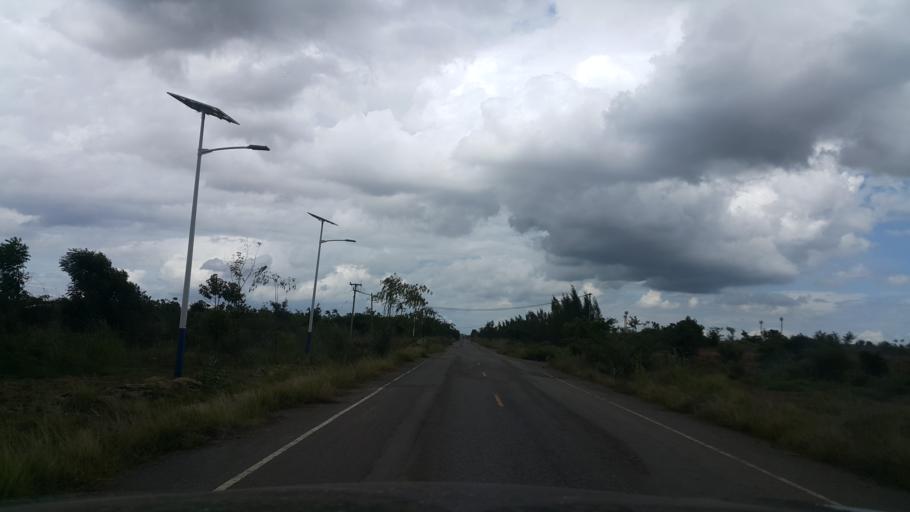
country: TH
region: Sukhothai
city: Sukhothai
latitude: 17.0617
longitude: 99.7852
